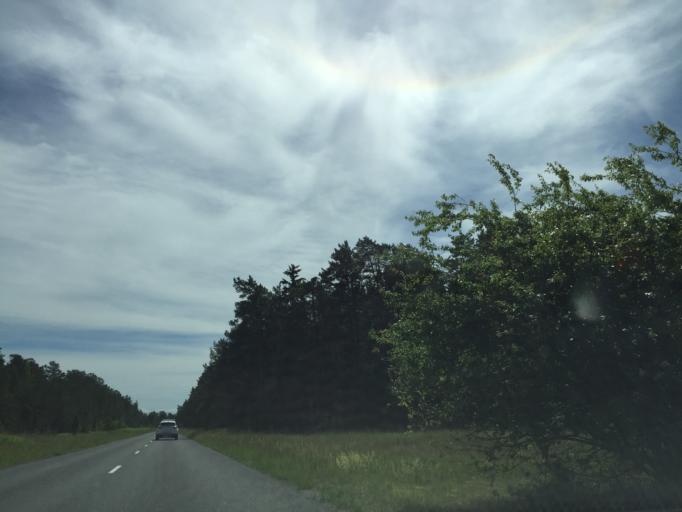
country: LV
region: Dundaga
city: Dundaga
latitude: 57.6664
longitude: 22.5703
